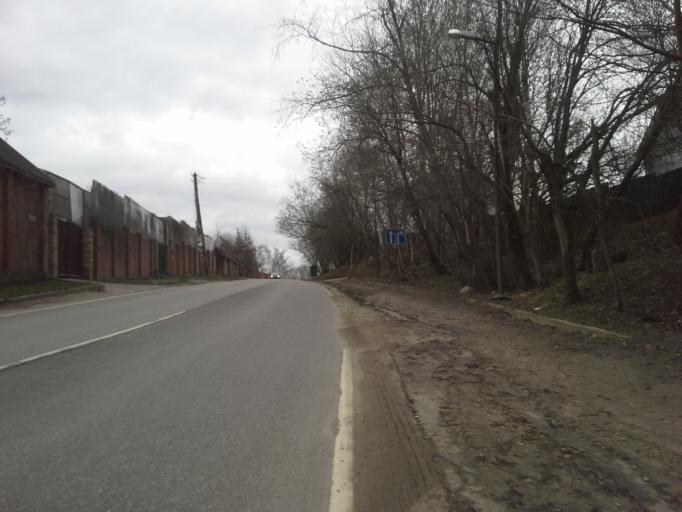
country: RU
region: Moskovskaya
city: Kommunarka
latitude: 55.5281
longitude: 37.4614
